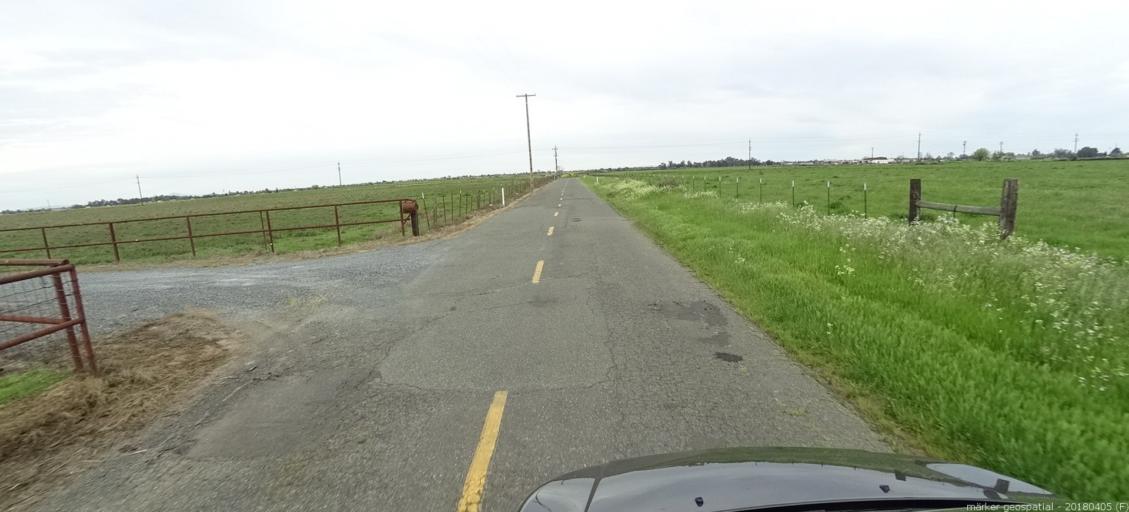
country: US
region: California
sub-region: Sacramento County
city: Herald
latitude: 38.2773
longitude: -121.2613
